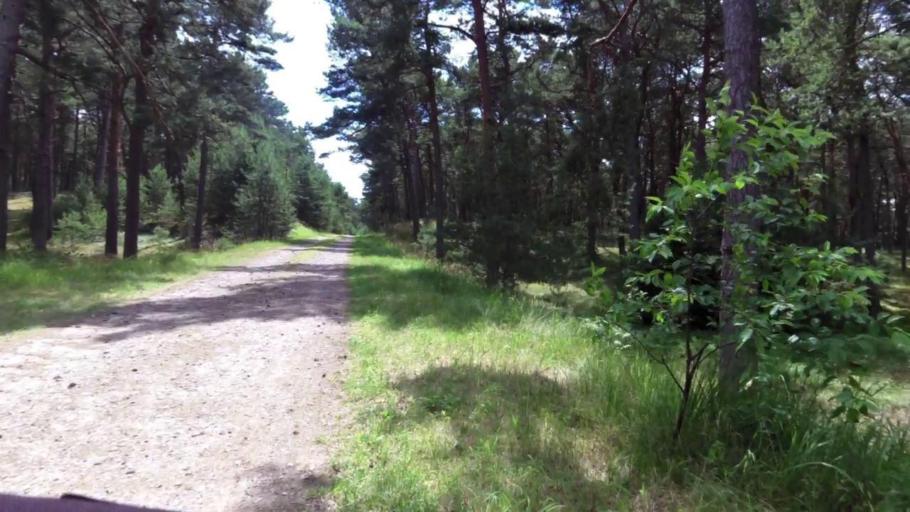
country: PL
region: West Pomeranian Voivodeship
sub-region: Powiat gryficki
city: Mrzezyno
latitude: 54.1268
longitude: 15.2205
